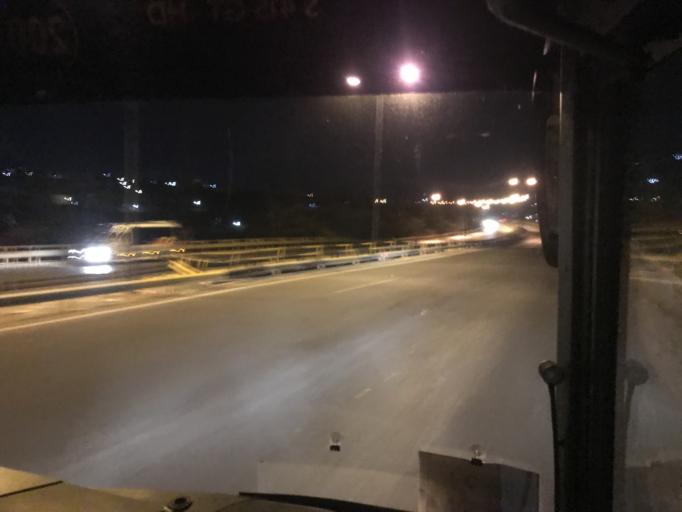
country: GR
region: Crete
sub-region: Nomos Irakleiou
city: Nea Alikarnassos
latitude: 35.3322
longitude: 25.1574
